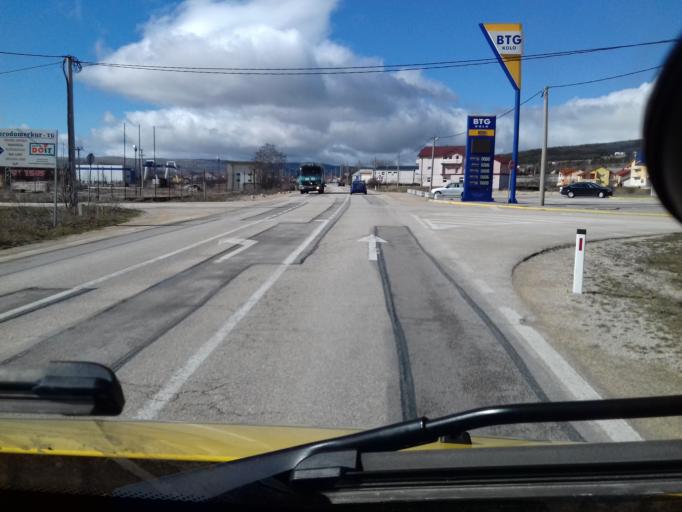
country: BA
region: Federation of Bosnia and Herzegovina
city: Tomislavgrad
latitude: 43.7068
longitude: 17.2309
